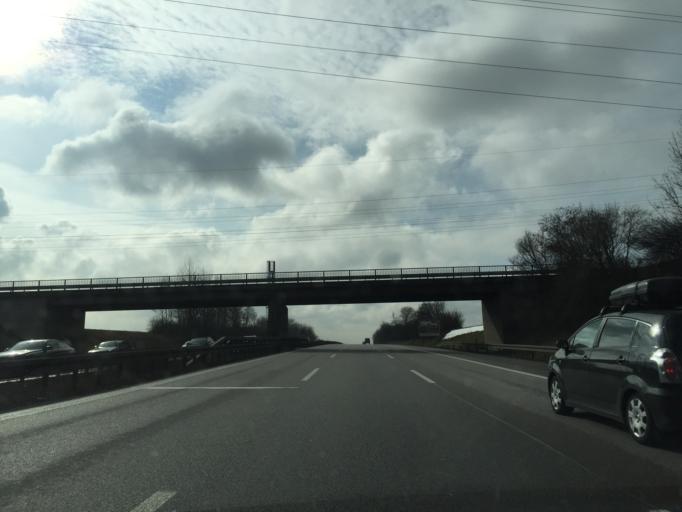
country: DE
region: Bavaria
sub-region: Upper Bavaria
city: Lenting
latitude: 48.8015
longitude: 11.4648
